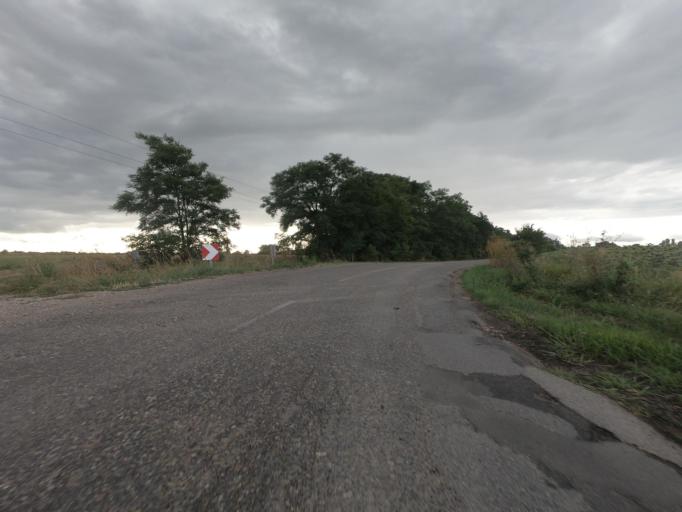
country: HU
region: Heves
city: Poroszlo
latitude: 47.6999
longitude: 20.6431
